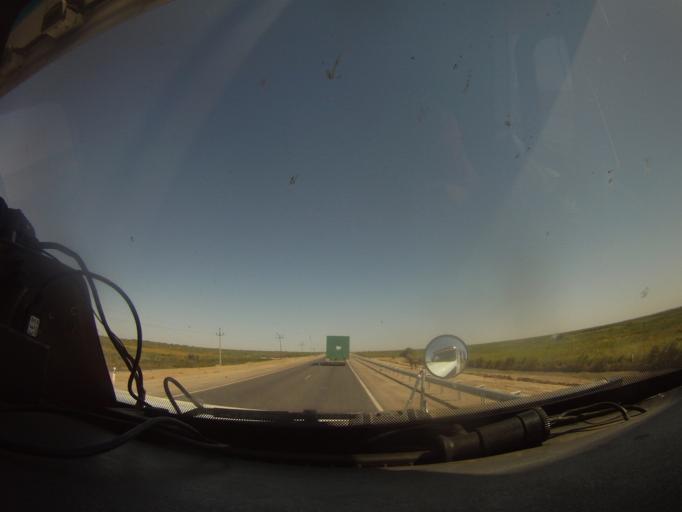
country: KZ
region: Qyzylorda
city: Terenozek
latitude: 44.8813
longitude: 65.0875
